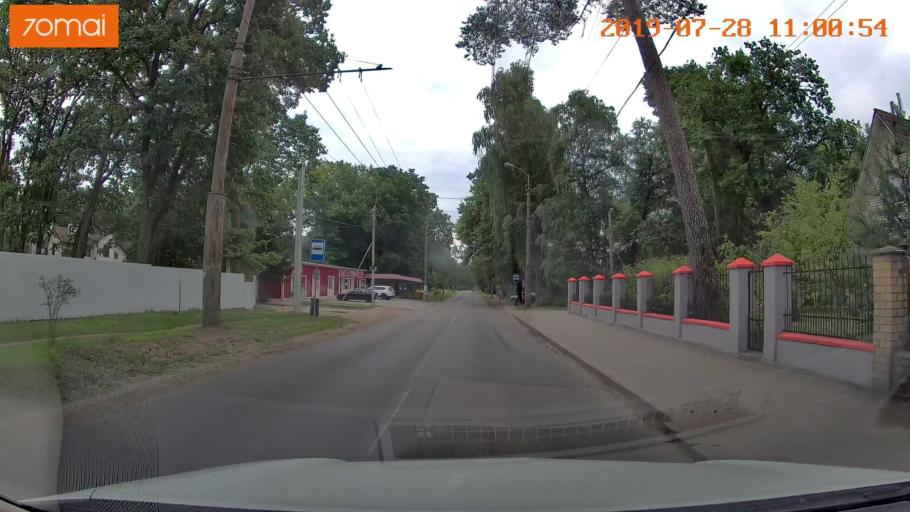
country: RU
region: Kaliningrad
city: Vzmorye
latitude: 54.7247
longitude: 20.3646
